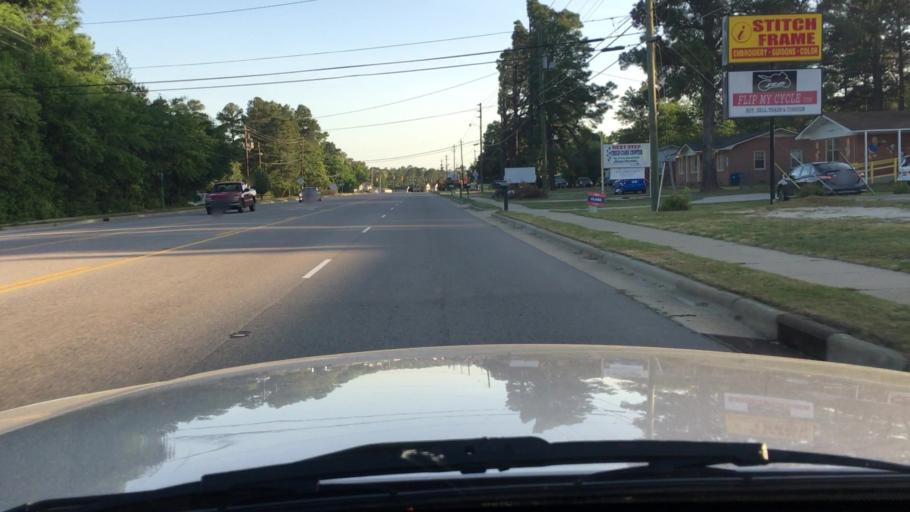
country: US
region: North Carolina
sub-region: Cumberland County
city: Fort Bragg
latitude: 35.0960
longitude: -79.0109
